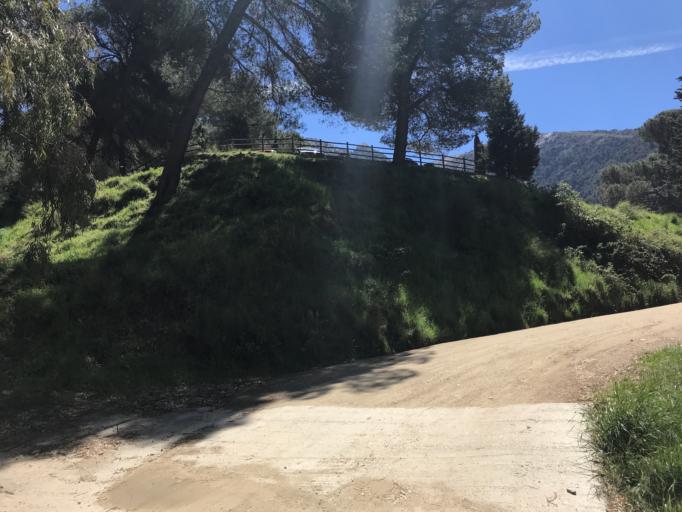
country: ES
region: Andalusia
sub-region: Provincia de Malaga
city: Alcaucin
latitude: 36.9185
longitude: -4.0893
